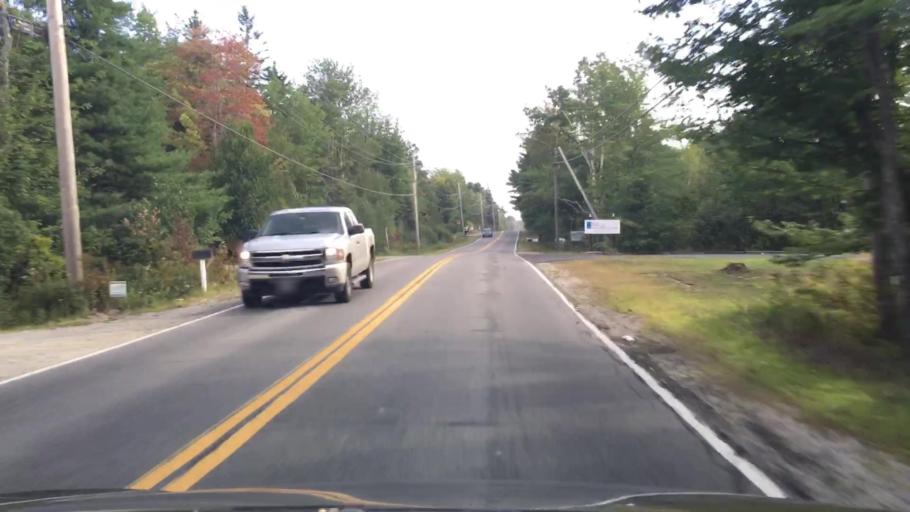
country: US
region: Maine
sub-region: Hancock County
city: Surry
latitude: 44.4374
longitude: -68.5713
